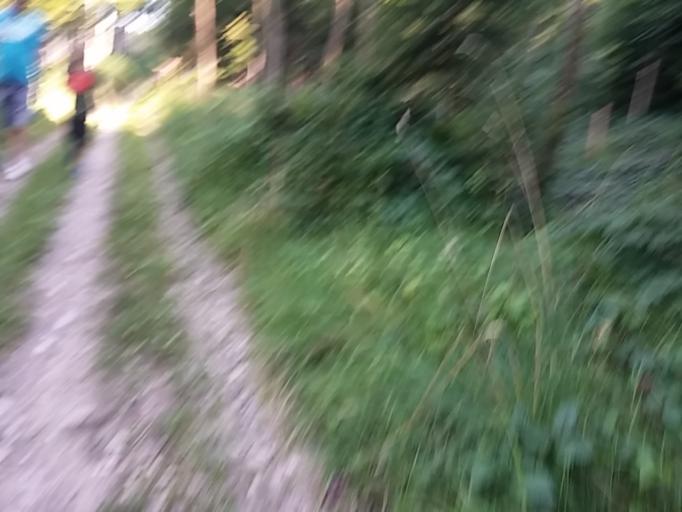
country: DE
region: Baden-Wuerttemberg
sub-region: Tuebingen Region
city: Leutkirch im Allgau
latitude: 47.7795
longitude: 10.0607
